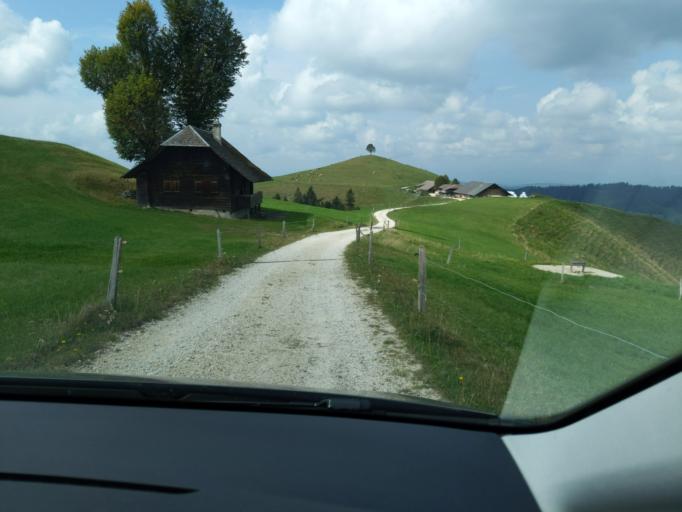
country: CH
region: Bern
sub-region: Oberaargau
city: Wyssachen
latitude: 47.0280
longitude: 7.8298
